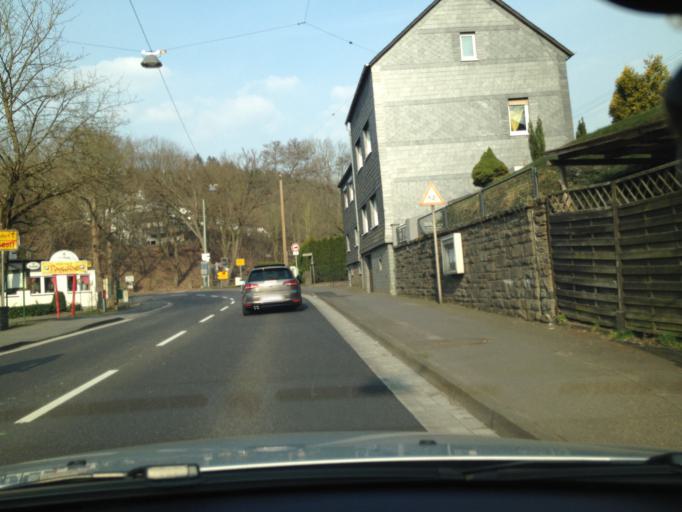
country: DE
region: Rheinland-Pfalz
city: Betzdorf
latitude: 50.7809
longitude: 7.8785
